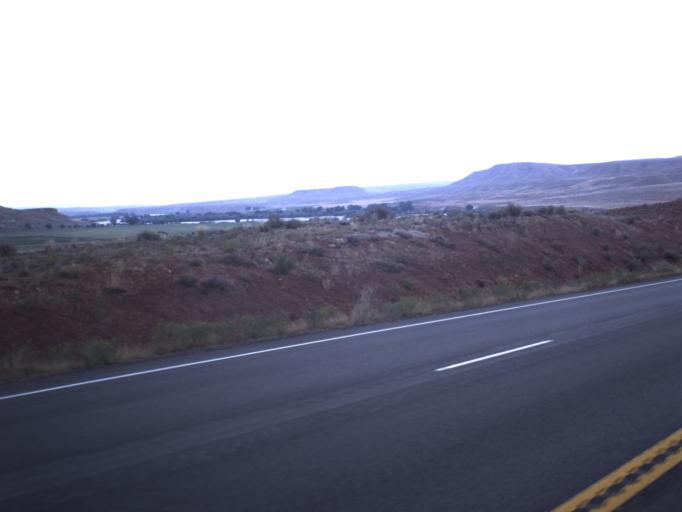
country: US
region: Utah
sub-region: Uintah County
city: Naples
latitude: 40.3225
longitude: -109.4865
